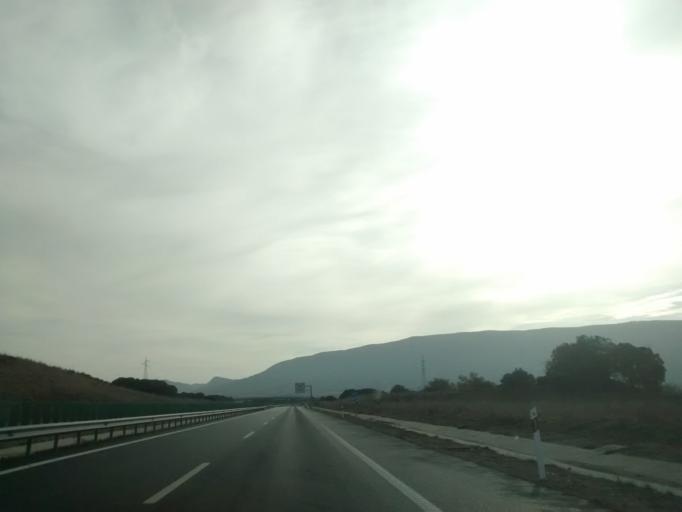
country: ES
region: Aragon
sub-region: Provincia de Zaragoza
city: Siguees
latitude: 42.6191
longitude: -1.0042
